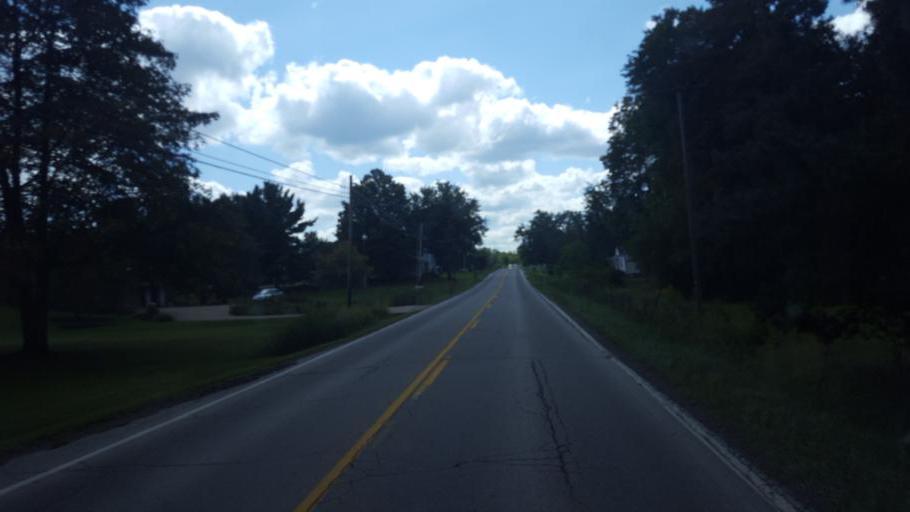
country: US
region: Ohio
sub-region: Ashland County
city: Ashland
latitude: 40.9170
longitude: -82.2815
